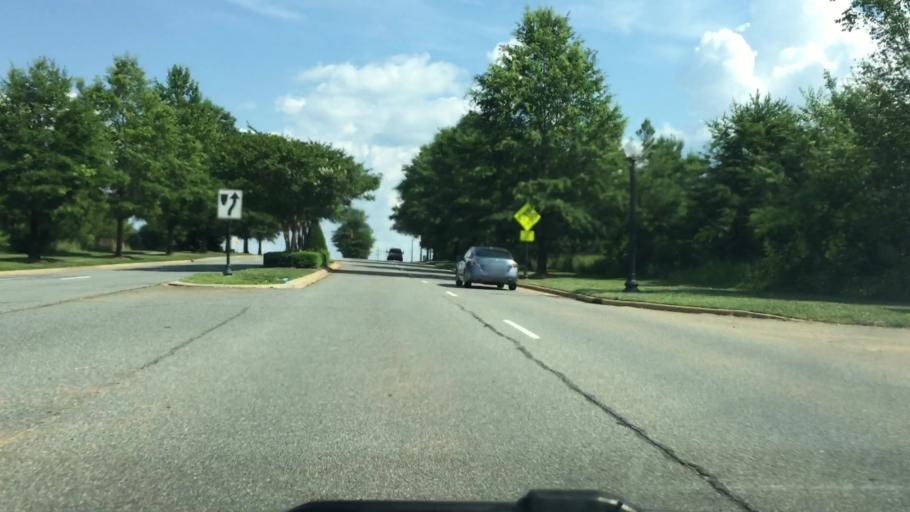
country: US
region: North Carolina
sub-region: Iredell County
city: Mooresville
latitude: 35.5836
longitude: -80.8823
